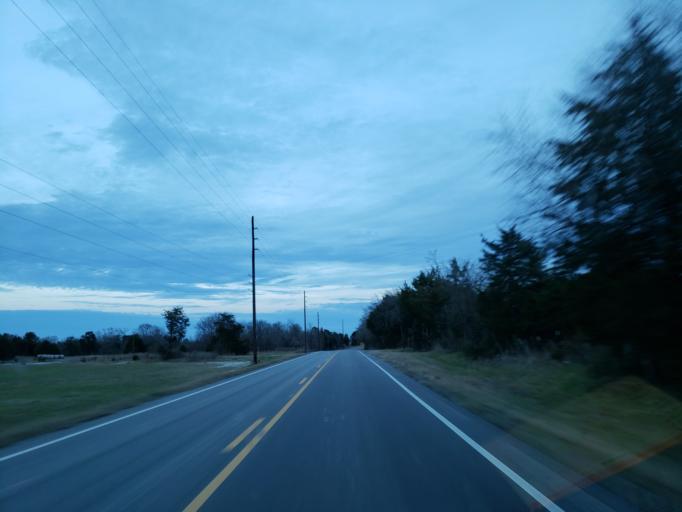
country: US
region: Alabama
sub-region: Sumter County
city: Livingston
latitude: 32.8114
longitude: -88.2832
